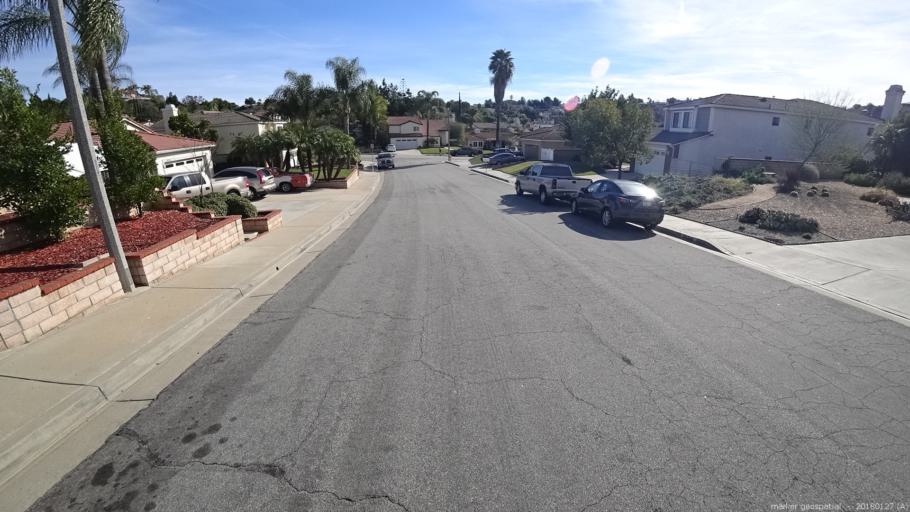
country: US
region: California
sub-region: Los Angeles County
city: Diamond Bar
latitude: 34.0333
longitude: -117.7920
